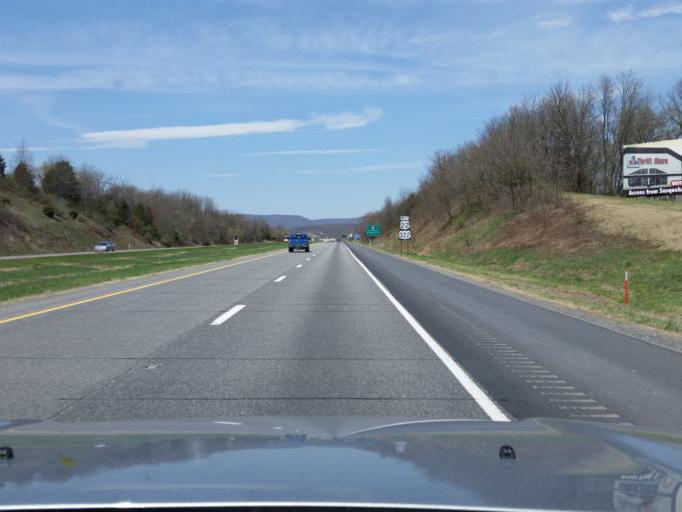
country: US
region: Pennsylvania
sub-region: Juniata County
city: Mifflintown
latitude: 40.5624
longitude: -77.3643
